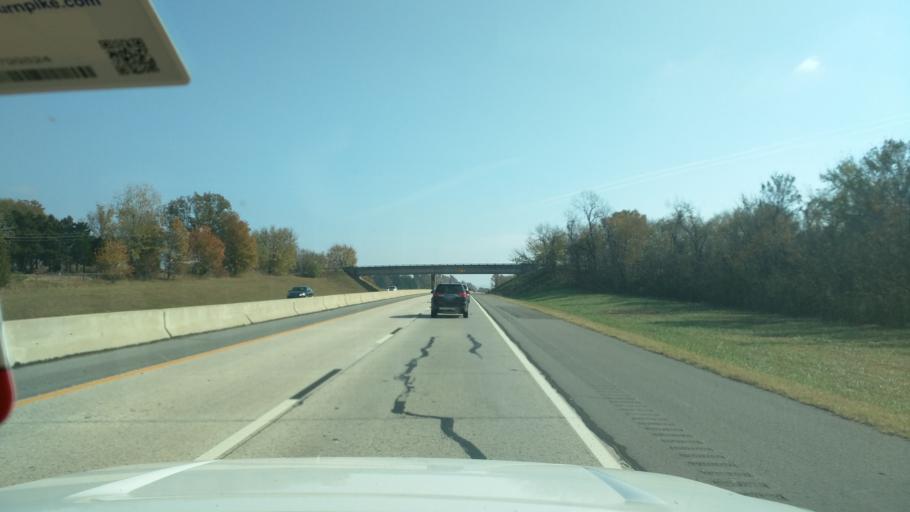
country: US
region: Oklahoma
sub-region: Muskogee County
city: Muskogee
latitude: 35.8285
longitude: -95.3498
